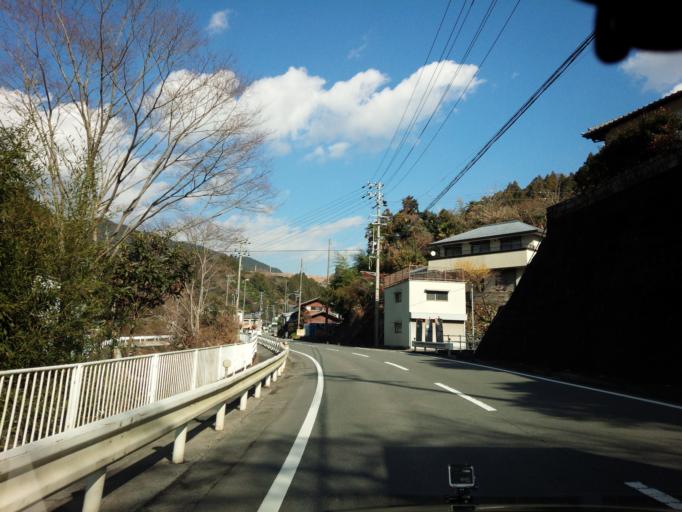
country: JP
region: Shizuoka
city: Fujinomiya
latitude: 35.1216
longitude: 138.5105
